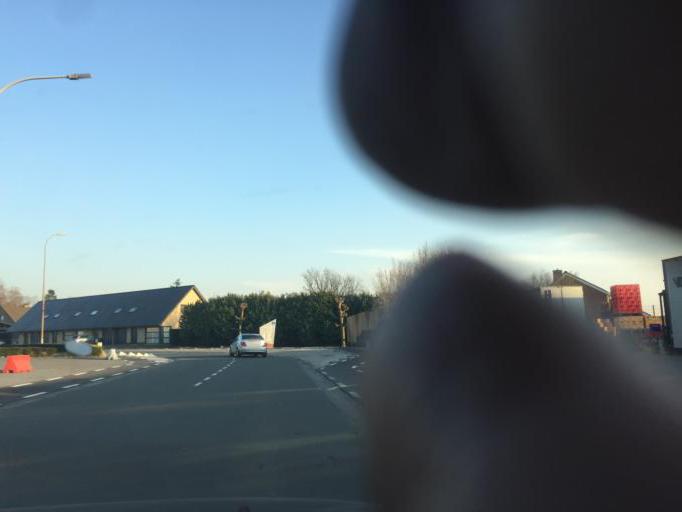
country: BE
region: Flanders
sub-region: Provincie West-Vlaanderen
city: Meulebeke
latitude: 50.9592
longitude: 3.2957
